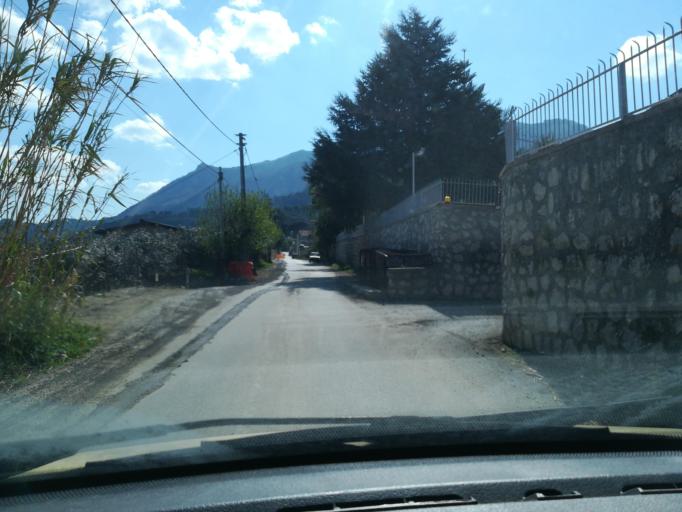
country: IT
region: Sicily
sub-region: Palermo
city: Cannizzaro-Favara
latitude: 38.0462
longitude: 13.2679
